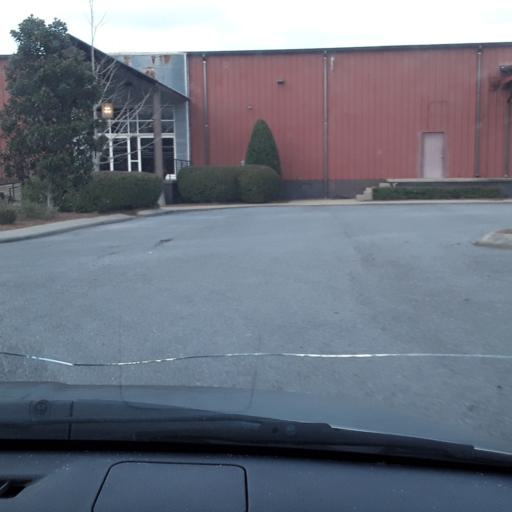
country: US
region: Tennessee
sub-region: Wilson County
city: Lebanon
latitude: 36.2115
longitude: -86.2939
